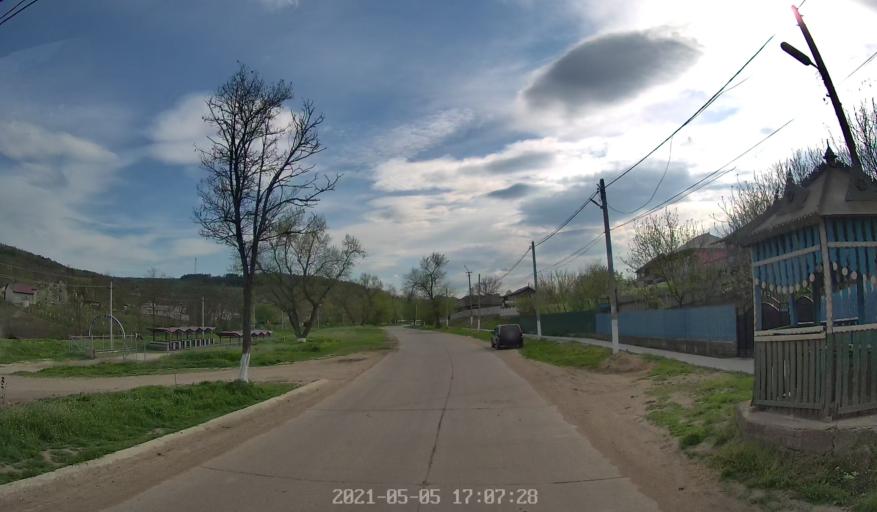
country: MD
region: Chisinau
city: Vadul lui Voda
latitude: 47.0127
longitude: 29.1343
